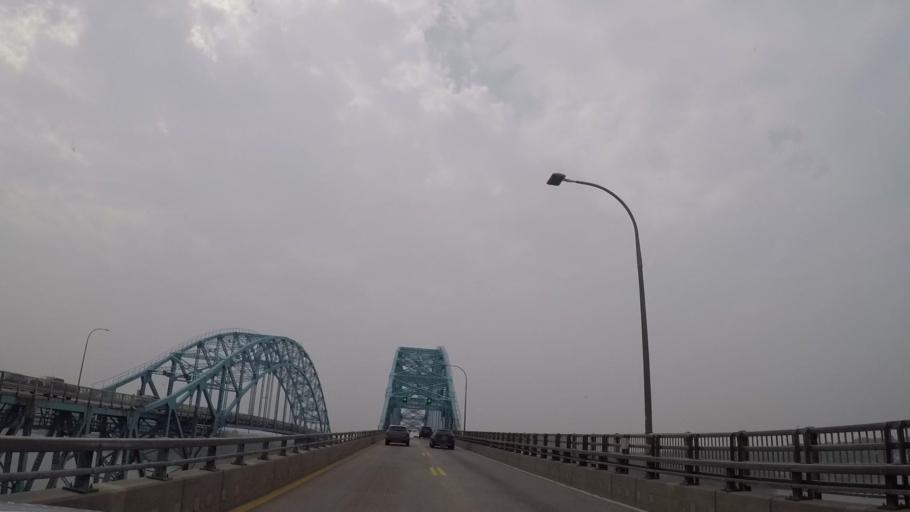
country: US
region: New York
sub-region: Erie County
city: Grandyle Village
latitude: 42.9978
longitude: -78.9353
